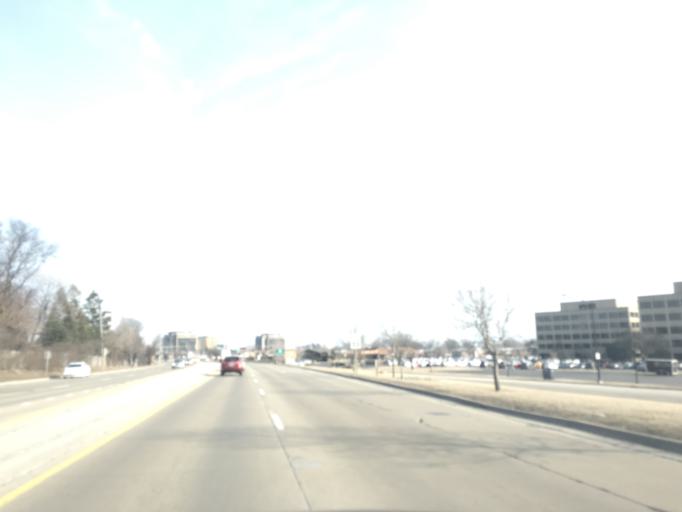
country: US
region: Illinois
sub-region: Cook County
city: Rolling Meadows
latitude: 42.0649
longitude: -88.0359
